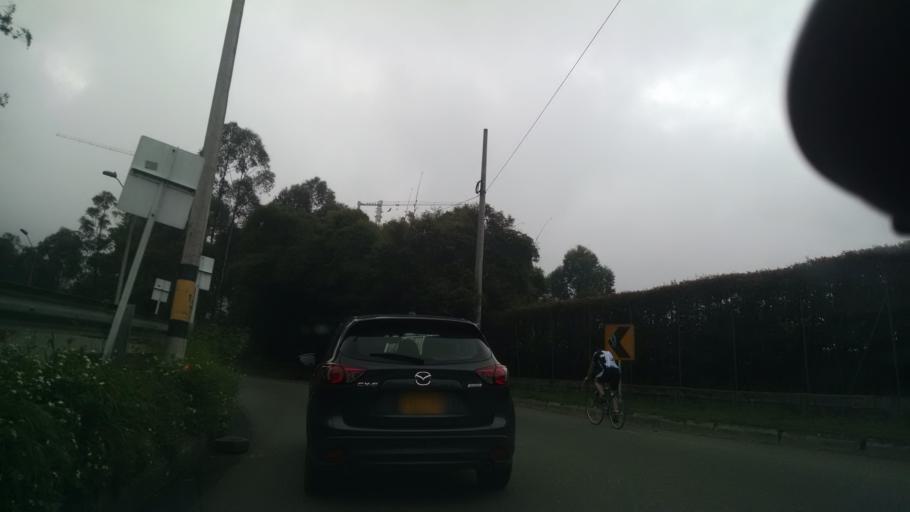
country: CO
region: Antioquia
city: Medellin
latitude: 6.2139
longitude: -75.5514
